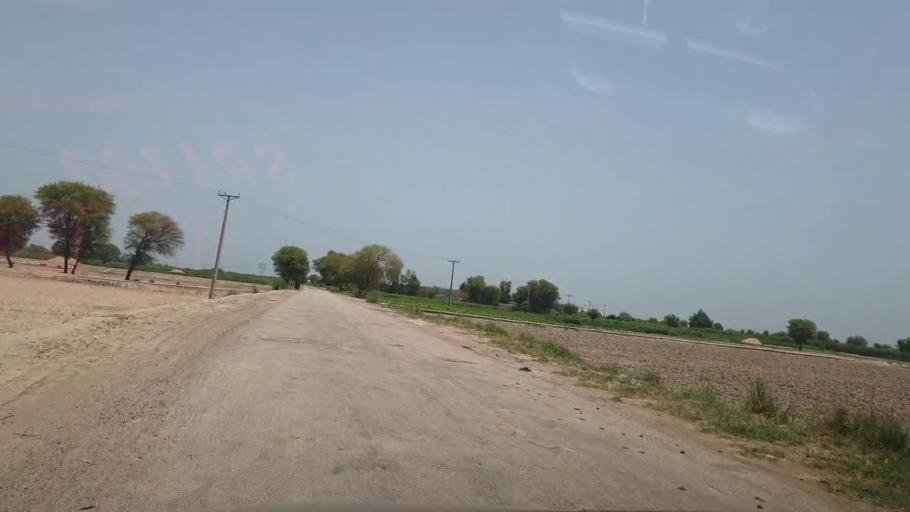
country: PK
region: Sindh
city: Daulatpur
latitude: 26.3894
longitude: 68.0695
